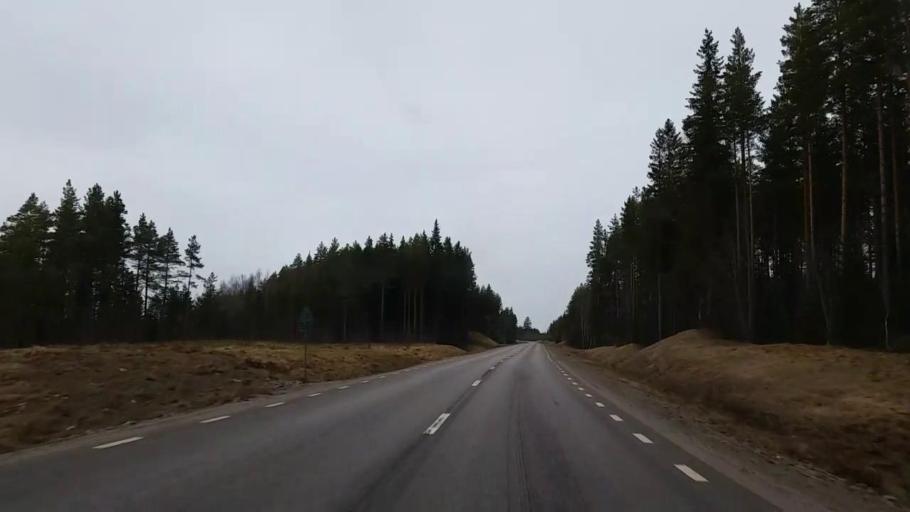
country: SE
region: Gaevleborg
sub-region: Ovanakers Kommun
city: Edsbyn
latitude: 61.1799
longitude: 15.8794
